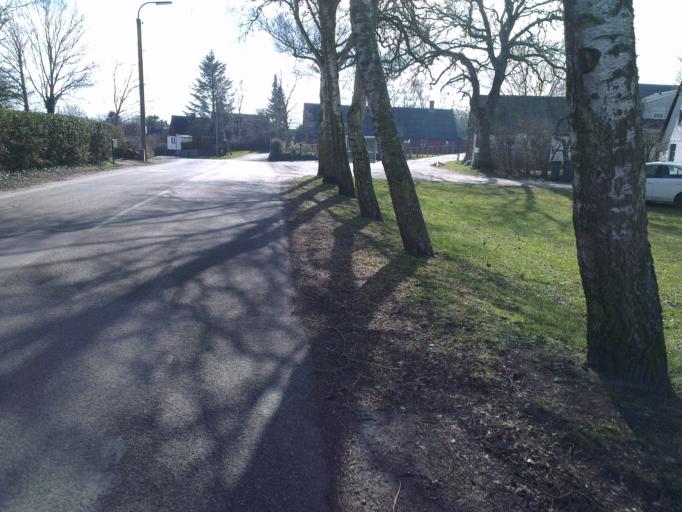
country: DK
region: Capital Region
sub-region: Frederikssund Kommune
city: Skibby
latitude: 55.7364
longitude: 12.0318
